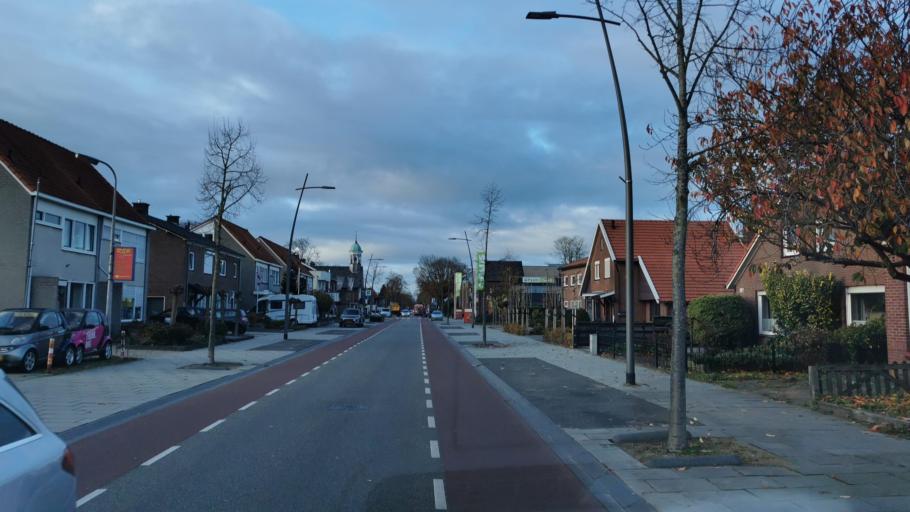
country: DE
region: North Rhine-Westphalia
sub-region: Regierungsbezirk Munster
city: Gronau
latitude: 52.2347
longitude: 7.0371
